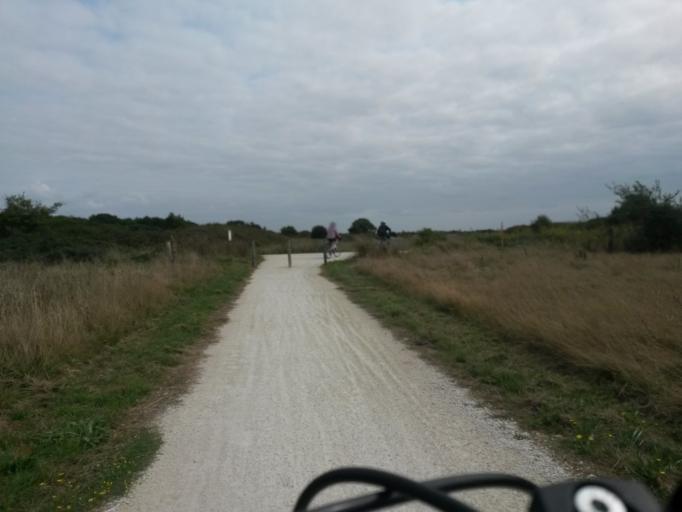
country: FR
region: Poitou-Charentes
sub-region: Departement de la Charente-Maritime
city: Dolus-d'Oleron
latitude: 45.8843
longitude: -1.2419
